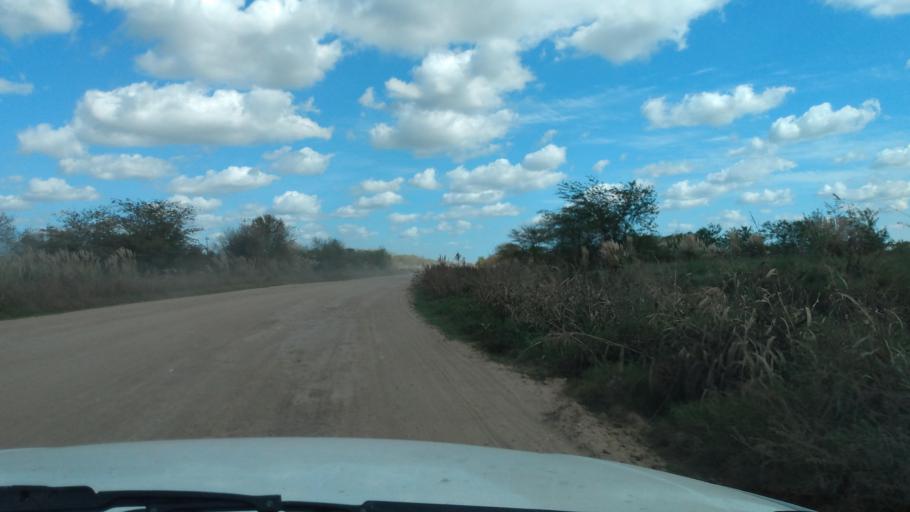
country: AR
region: Buenos Aires
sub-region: Partido de Navarro
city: Navarro
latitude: -34.9978
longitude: -59.3195
